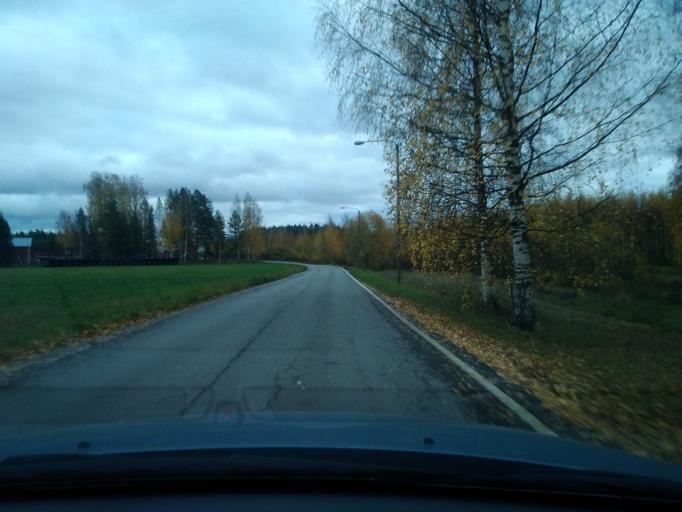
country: FI
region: Central Finland
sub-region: Saarijaervi-Viitasaari
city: Saarijaervi
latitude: 62.6892
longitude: 25.3162
